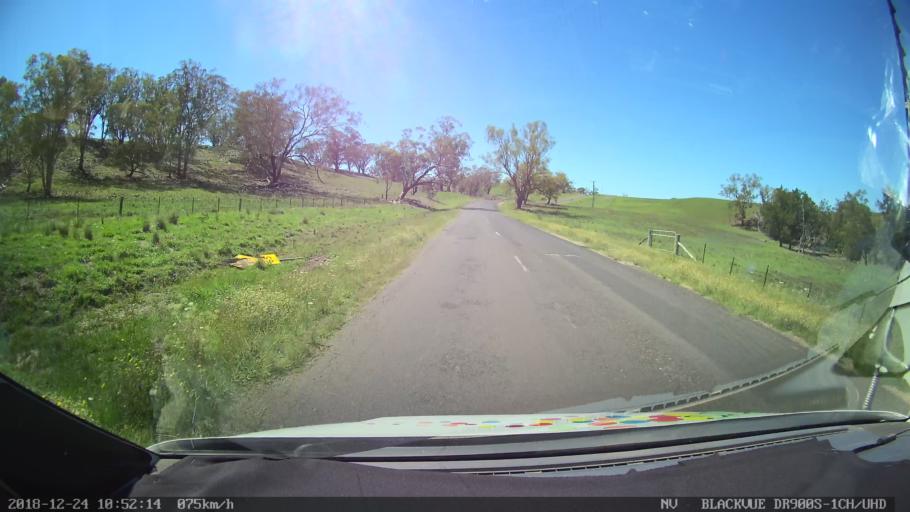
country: AU
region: New South Wales
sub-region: Upper Hunter Shire
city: Merriwa
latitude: -31.9783
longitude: 150.4215
